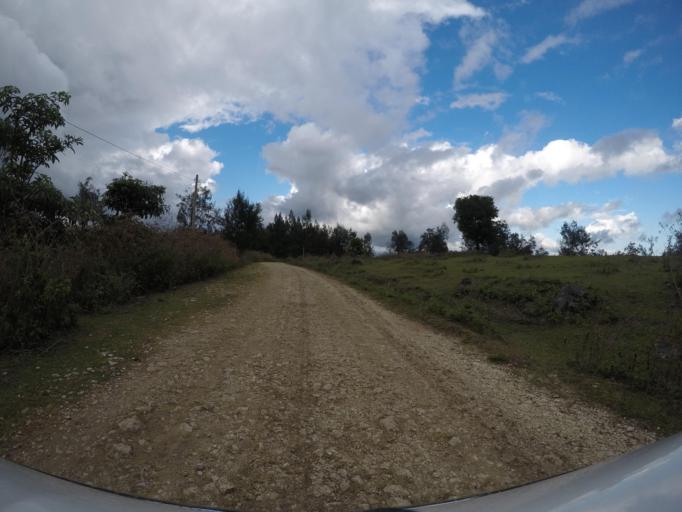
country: TL
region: Baucau
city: Venilale
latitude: -8.6806
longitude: 126.6400
